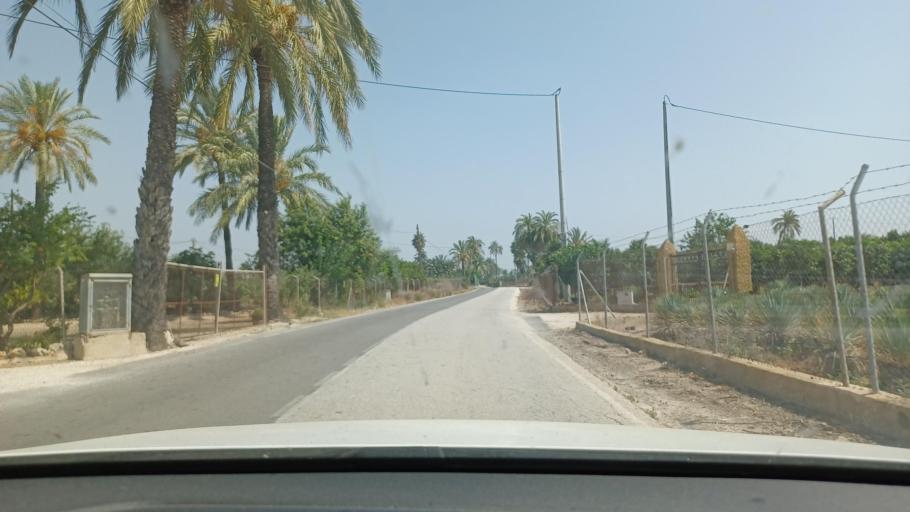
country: ES
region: Valencia
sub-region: Provincia de Alicante
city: Elche
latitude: 38.2347
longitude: -0.6932
